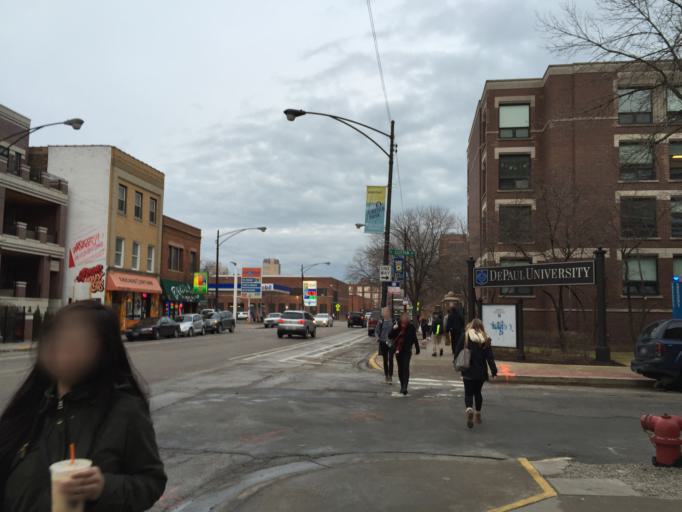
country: US
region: Illinois
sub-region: Cook County
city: Chicago
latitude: 41.9252
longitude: -87.6569
